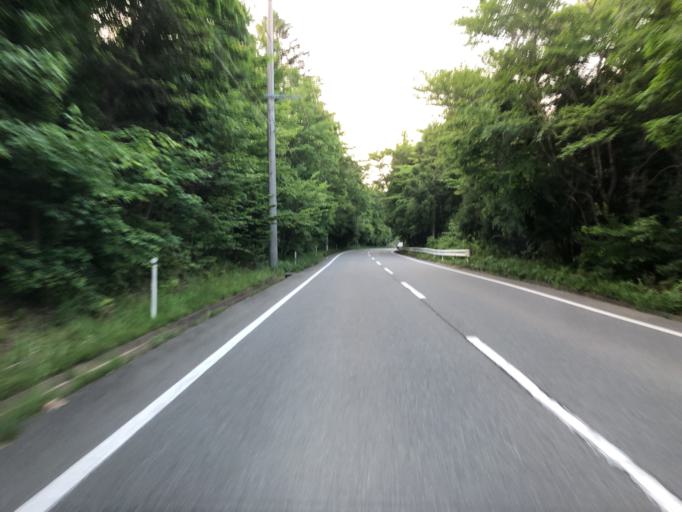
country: JP
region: Fukushima
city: Iwaki
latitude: 37.2554
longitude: 140.9695
